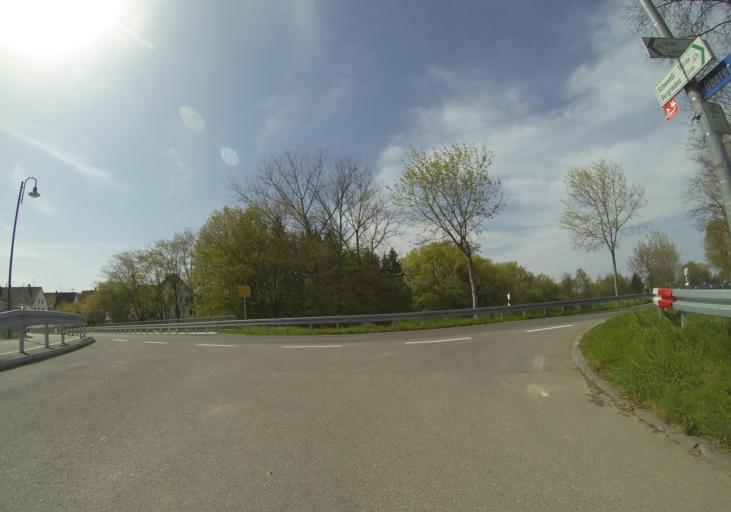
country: DE
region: Baden-Wuerttemberg
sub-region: Tuebingen Region
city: Achstetten
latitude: 48.2475
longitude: 9.9108
